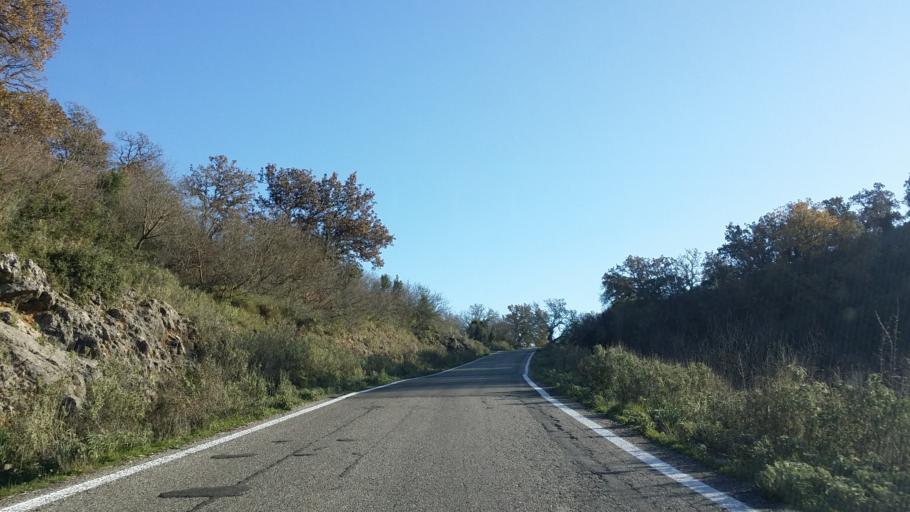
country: GR
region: West Greece
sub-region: Nomos Aitolias kai Akarnanias
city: Fitiai
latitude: 38.6374
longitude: 21.1917
